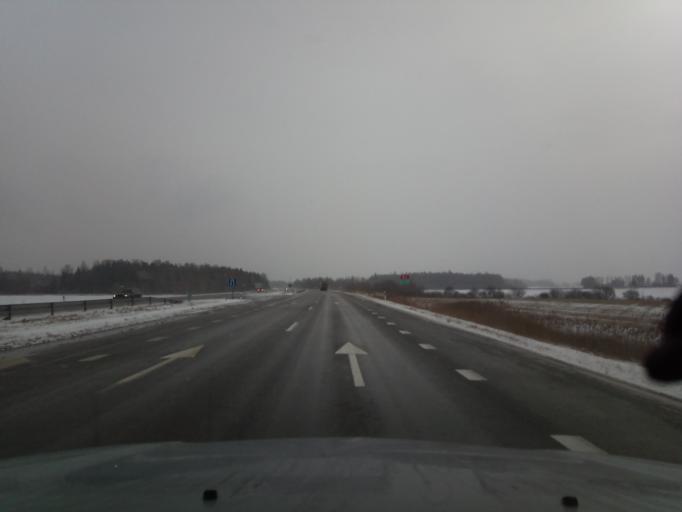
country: LT
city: Ramygala
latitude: 55.5390
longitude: 24.5385
